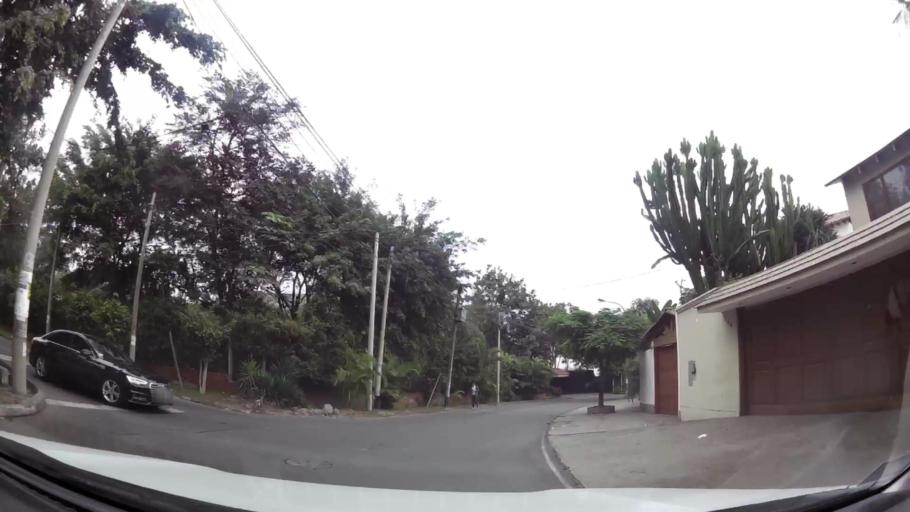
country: PE
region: Lima
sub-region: Lima
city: La Molina
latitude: -12.0766
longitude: -76.9075
